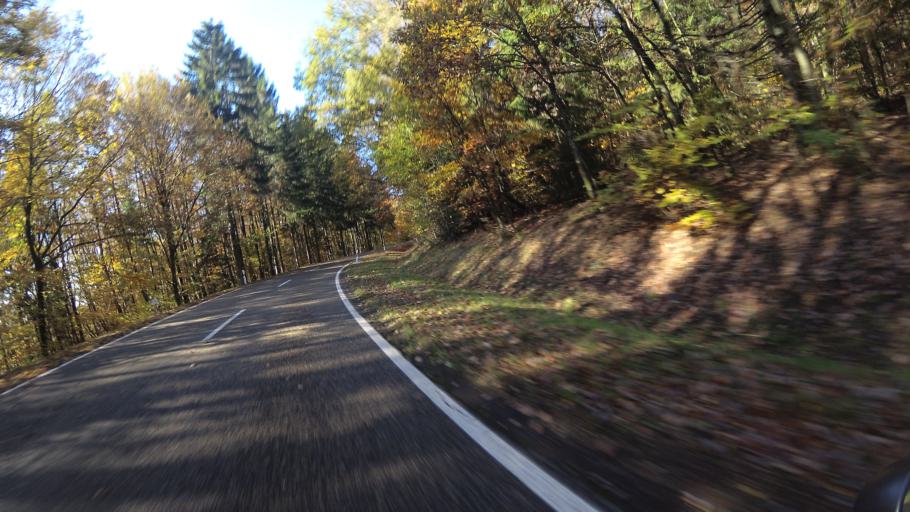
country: DE
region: Saarland
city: Losheim
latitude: 49.5509
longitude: 6.7510
